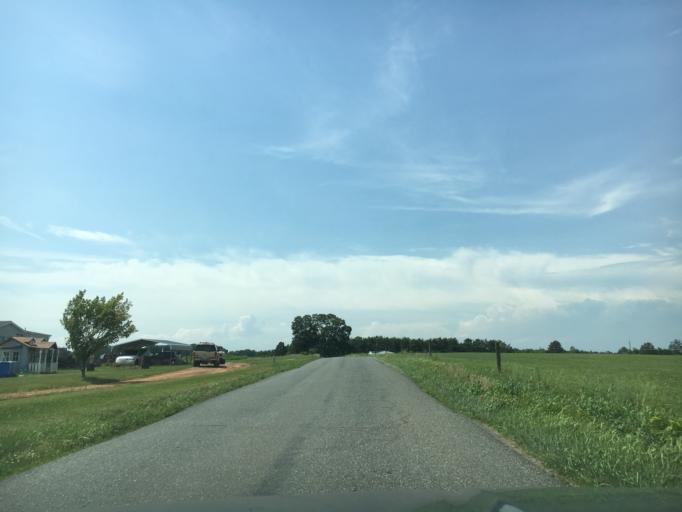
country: US
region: Virginia
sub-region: Pittsylvania County
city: Gretna
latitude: 36.9266
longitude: -79.4301
